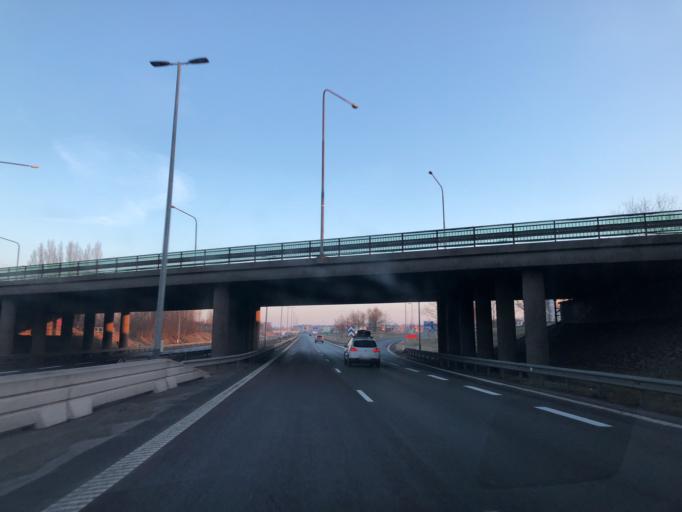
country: SE
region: Halland
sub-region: Halmstads Kommun
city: Fyllinge
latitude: 56.6532
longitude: 12.9051
